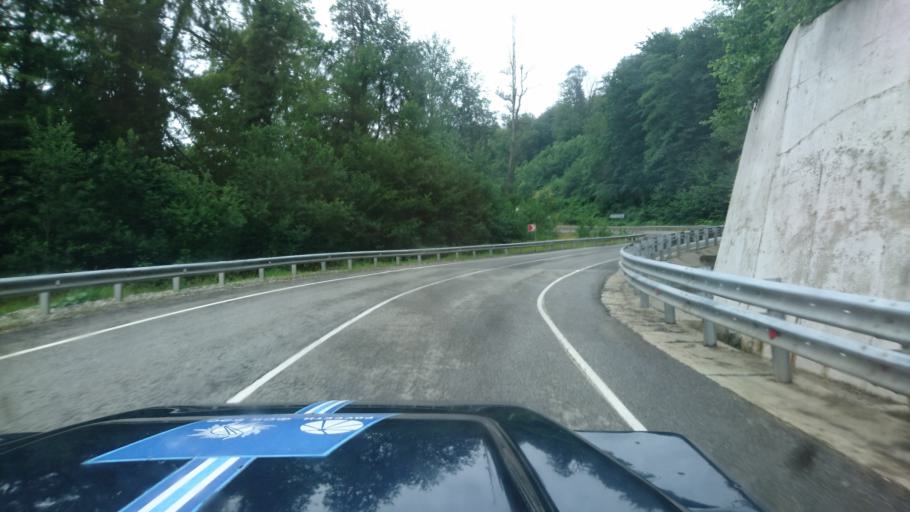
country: RU
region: Krasnodarskiy
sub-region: Sochi City
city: Krasnaya Polyana
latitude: 43.6665
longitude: 40.2942
